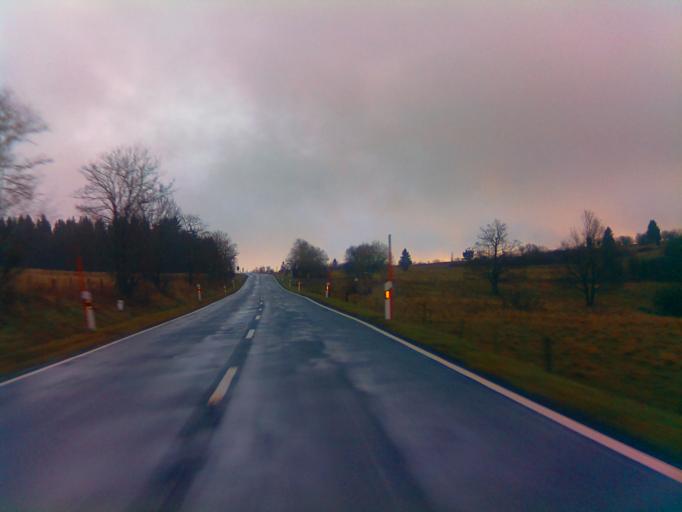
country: DE
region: Bavaria
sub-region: Regierungsbezirk Unterfranken
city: Bischofsheim an der Rhon
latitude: 50.4712
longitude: 10.0144
